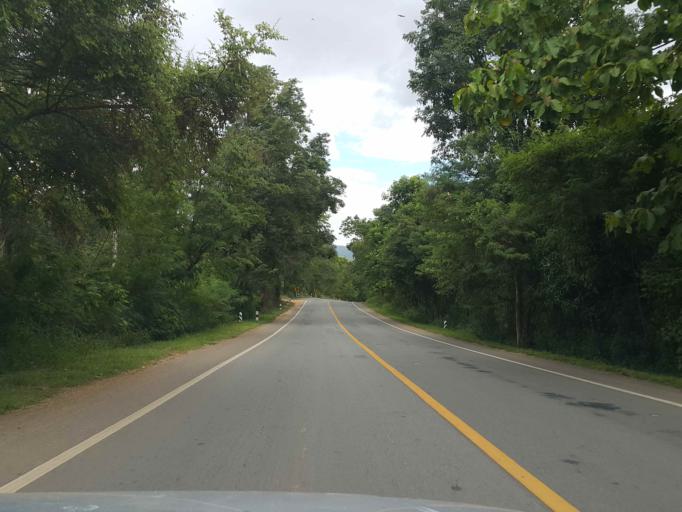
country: TH
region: Lamphun
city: Thung Hua Chang
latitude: 17.9725
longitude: 98.8808
